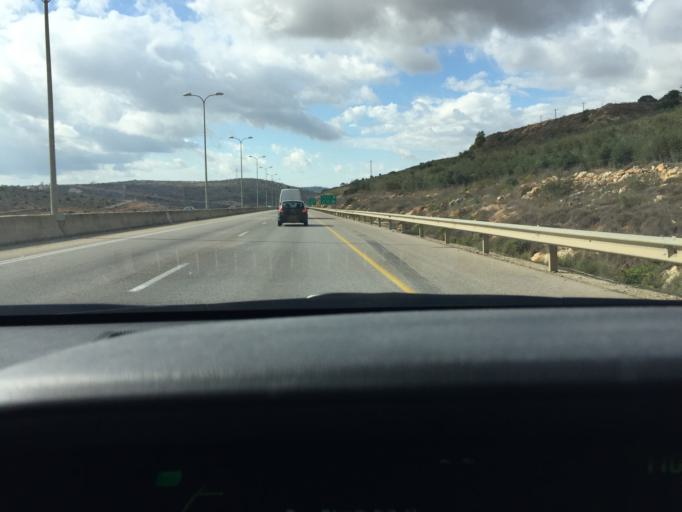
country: PS
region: West Bank
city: Sartah
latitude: 32.0976
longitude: 35.1161
